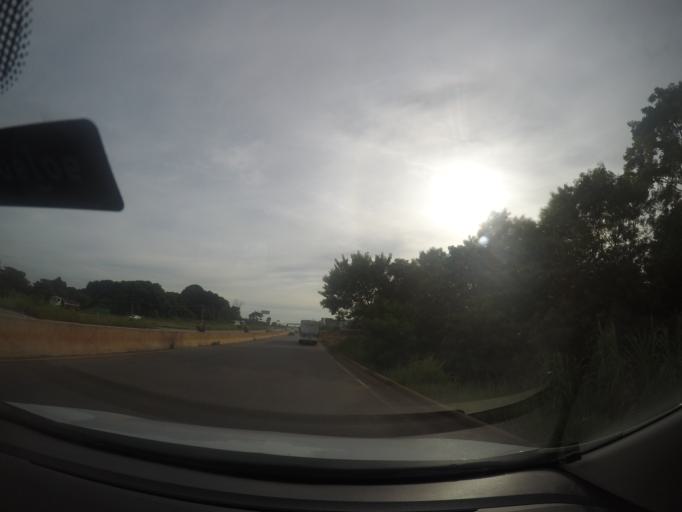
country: BR
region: Goias
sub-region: Goiania
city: Goiania
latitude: -16.7103
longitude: -49.3531
